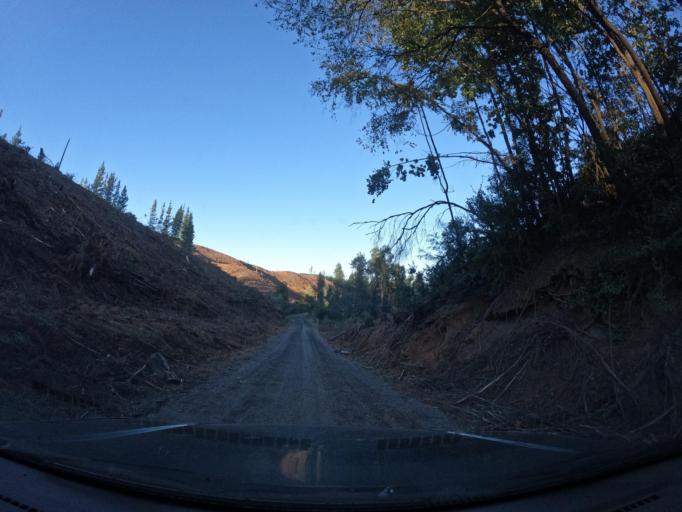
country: CL
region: Biobio
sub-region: Provincia de Concepcion
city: Chiguayante
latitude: -37.0384
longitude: -72.8360
